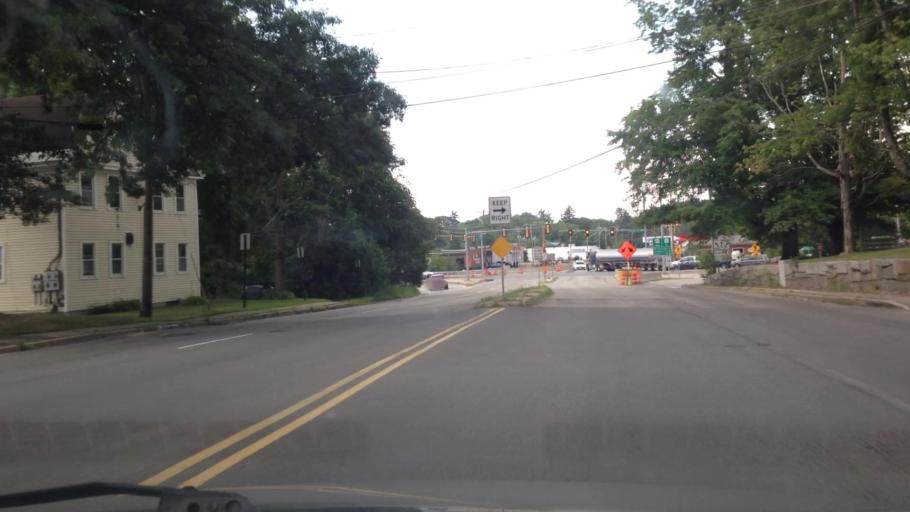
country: US
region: New Hampshire
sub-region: Cheshire County
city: Keene
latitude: 42.9227
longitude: -72.2765
